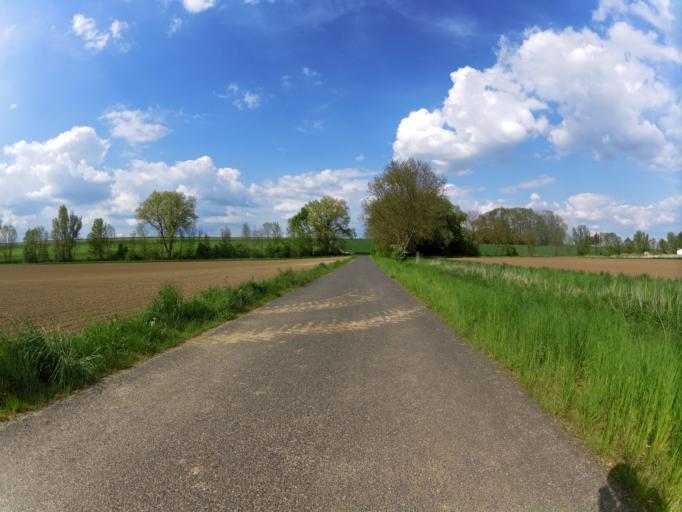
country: DE
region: Bavaria
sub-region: Regierungsbezirk Unterfranken
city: Giebelstadt
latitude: 49.6229
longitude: 9.9376
